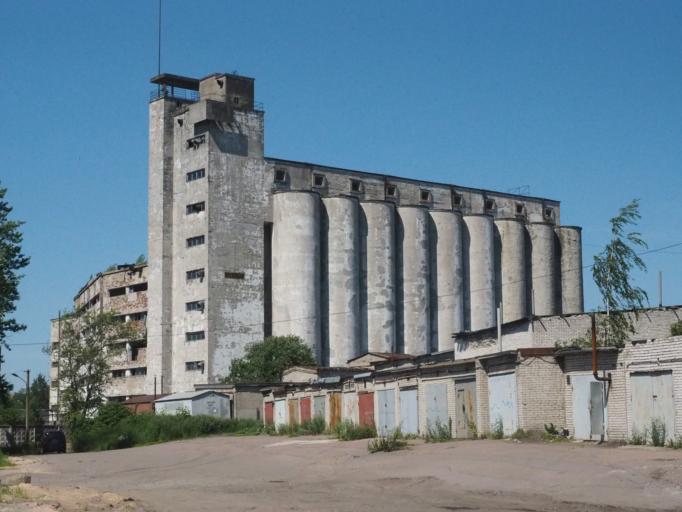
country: RU
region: Leningrad
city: Vyborg
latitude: 60.7055
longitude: 28.7393
